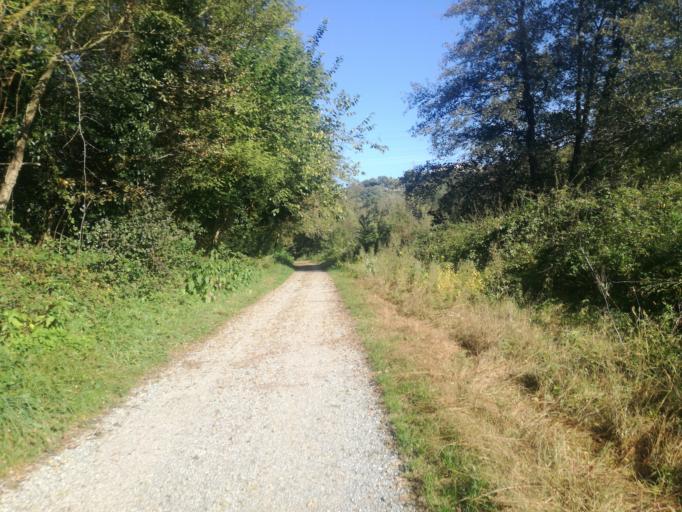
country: IT
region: Lombardy
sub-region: Provincia di Bergamo
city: Bottanuco
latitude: 45.6356
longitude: 9.4944
